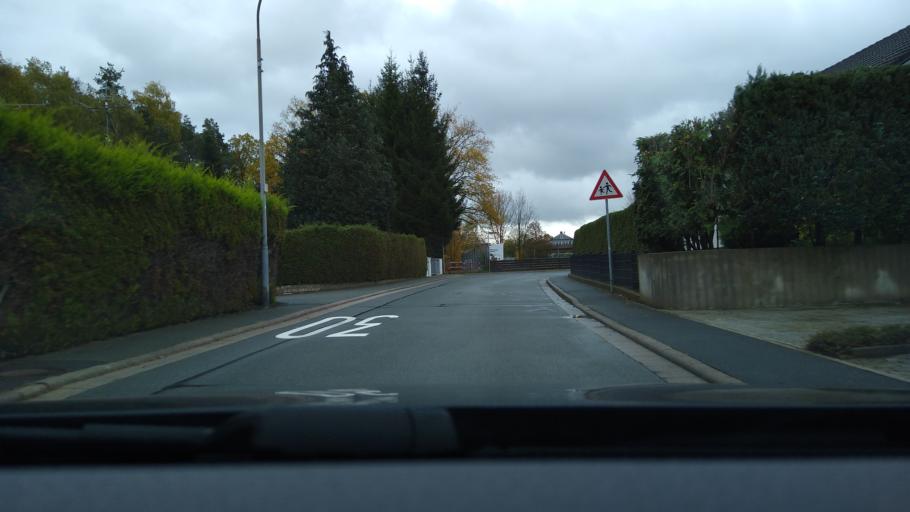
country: DE
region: Bavaria
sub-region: Regierungsbezirk Mittelfranken
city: Hemhofen
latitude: 49.6958
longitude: 10.9391
